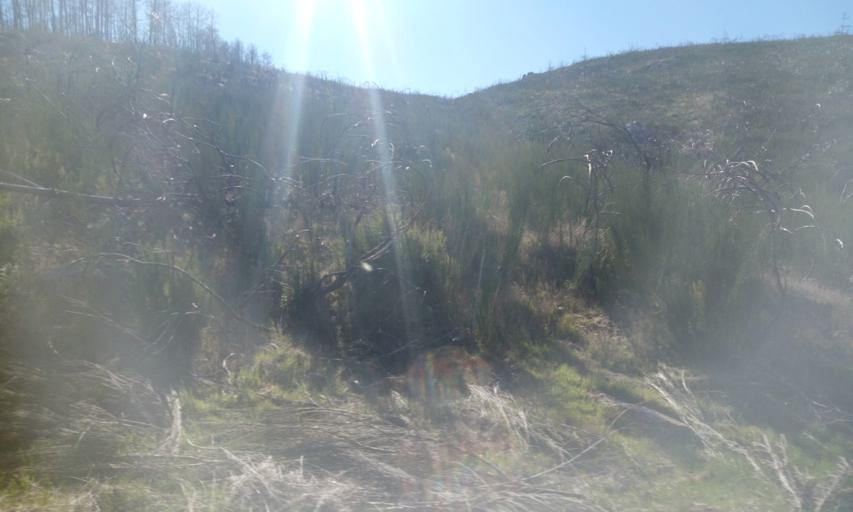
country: PT
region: Guarda
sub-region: Manteigas
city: Manteigas
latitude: 40.4901
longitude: -7.5404
